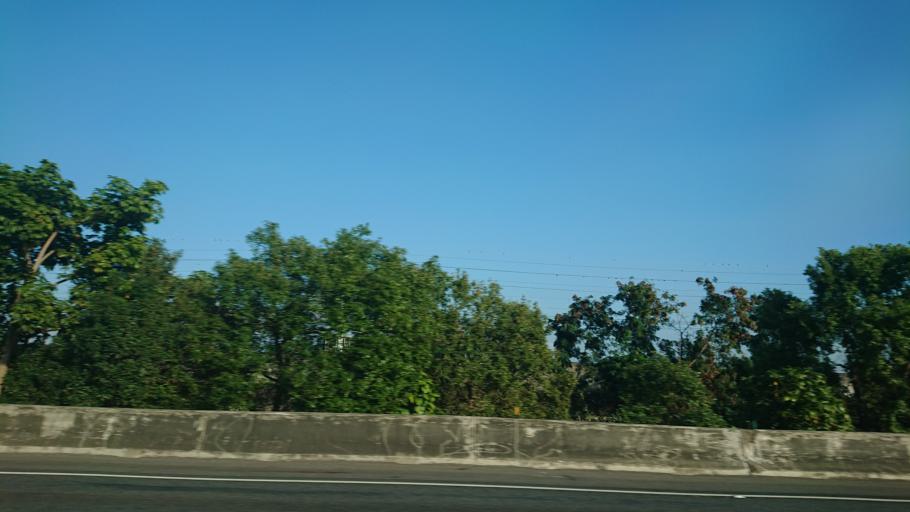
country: TW
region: Taiwan
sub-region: Taichung City
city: Taichung
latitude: 24.1361
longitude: 120.6178
